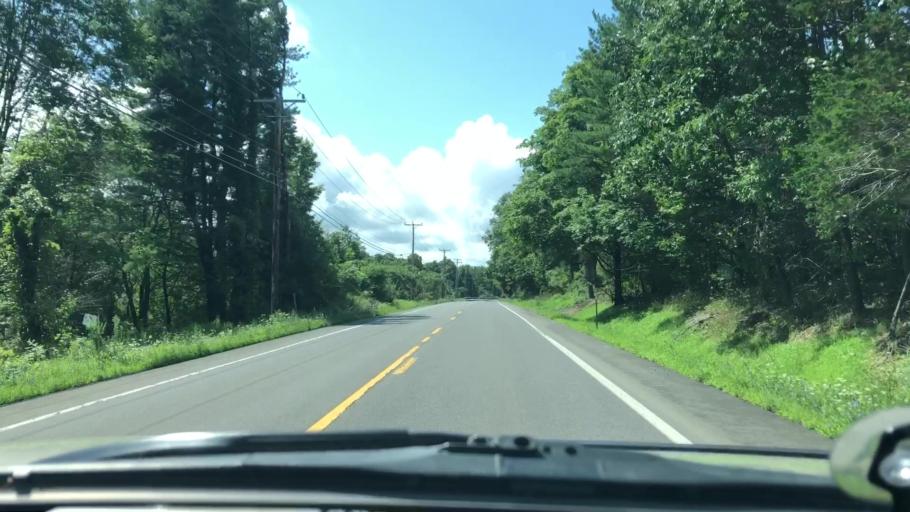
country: US
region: New York
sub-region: Greene County
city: Cairo
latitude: 42.2326
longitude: -73.9829
